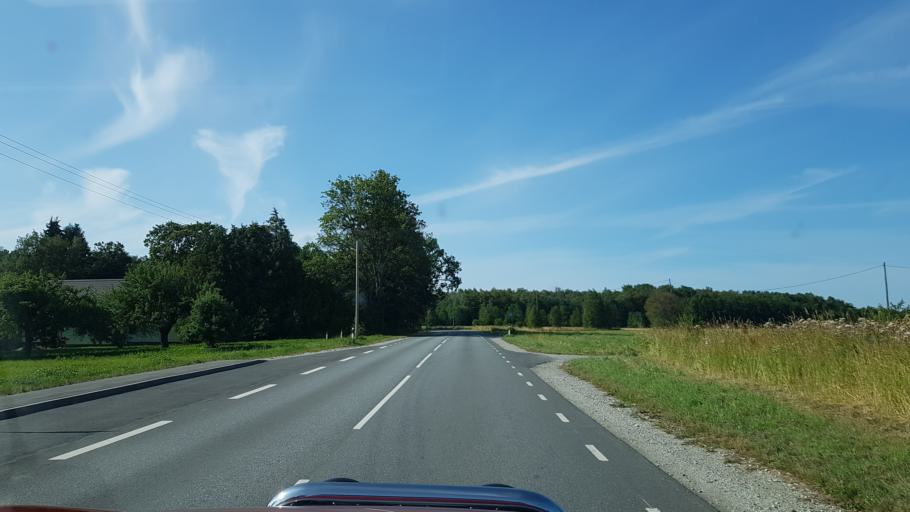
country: EE
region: Harju
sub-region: Rae vald
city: Jueri
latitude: 59.3826
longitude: 24.9286
